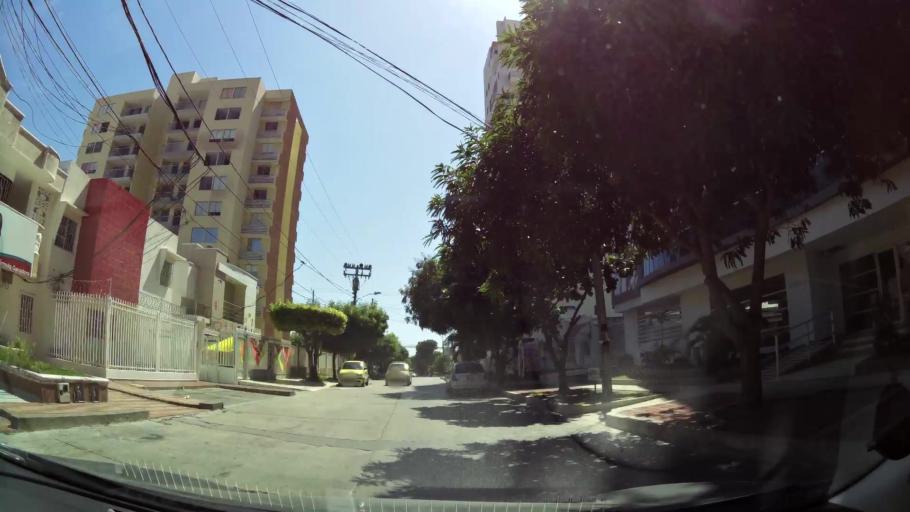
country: CO
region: Atlantico
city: Barranquilla
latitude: 11.0079
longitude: -74.7975
